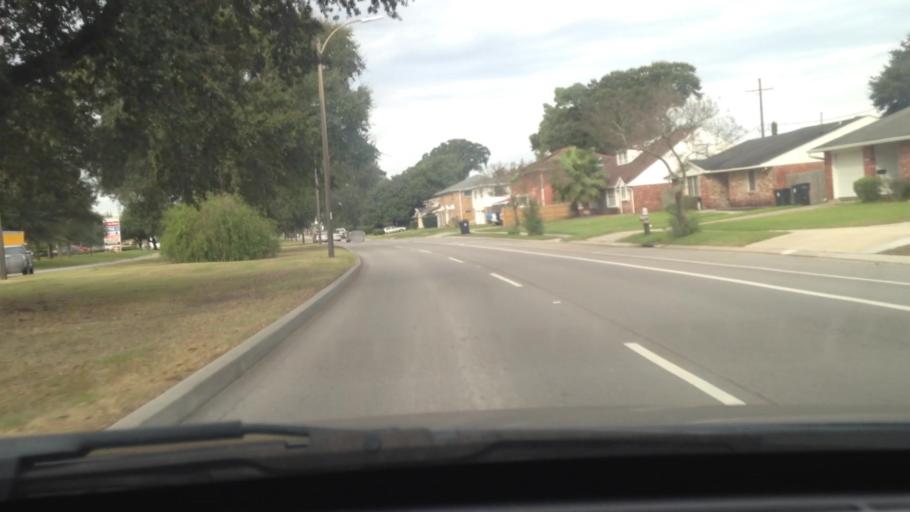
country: US
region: Louisiana
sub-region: Jefferson Parish
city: Terrytown
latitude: 29.9243
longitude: -90.0103
